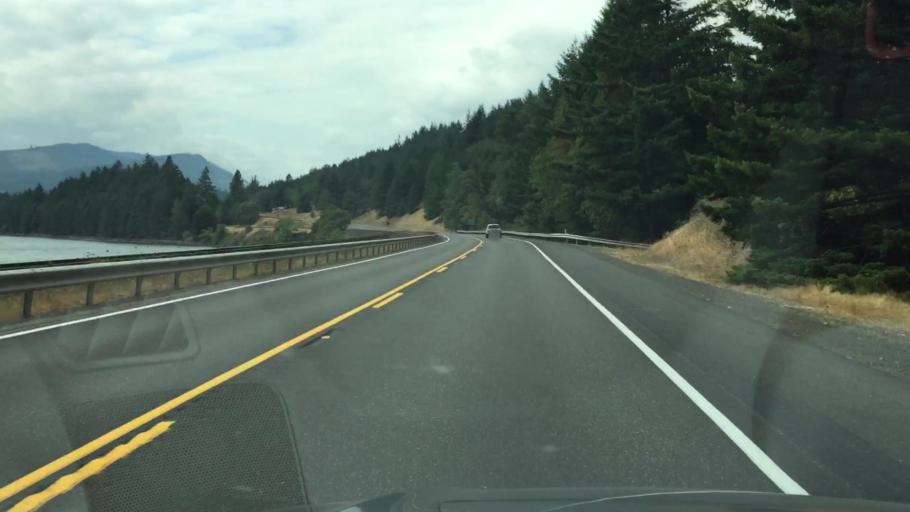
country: US
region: Washington
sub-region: Skamania County
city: Carson
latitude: 45.7055
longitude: -121.7628
